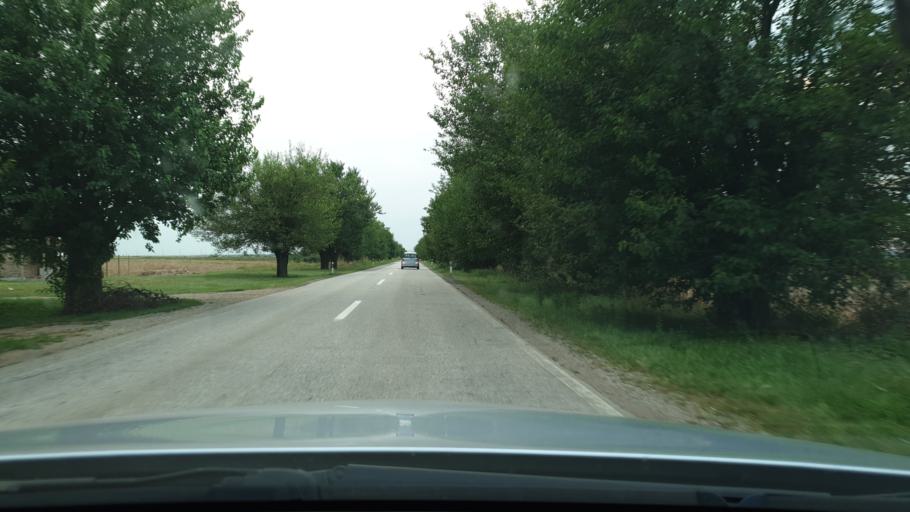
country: RS
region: Autonomna Pokrajina Vojvodina
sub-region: Juznobanatski Okrug
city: Vrsac
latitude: 45.0837
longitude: 21.2937
